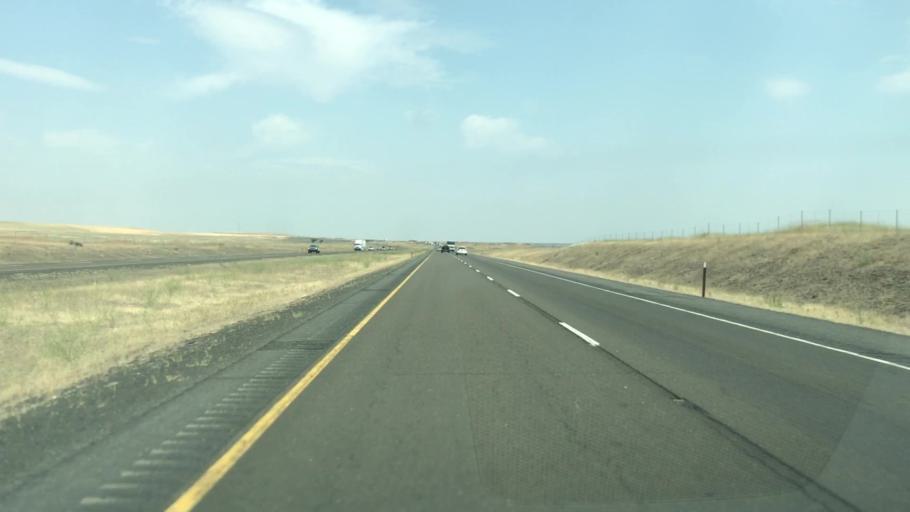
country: US
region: Washington
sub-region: Adams County
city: Ritzville
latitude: 47.2400
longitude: -118.1293
